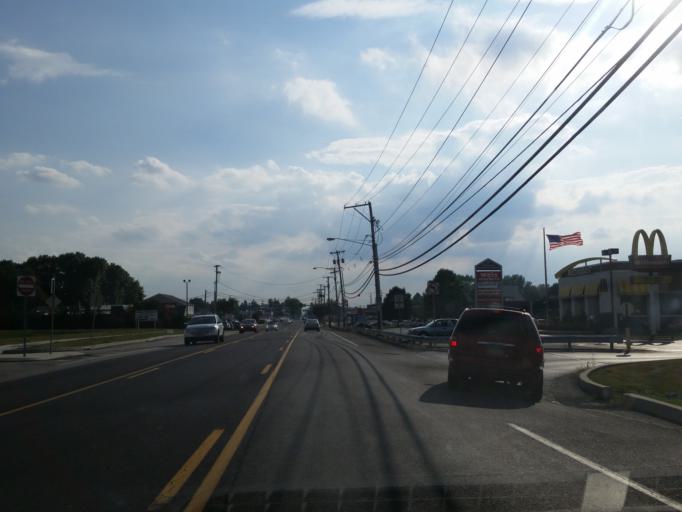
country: US
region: Pennsylvania
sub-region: Lebanon County
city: Palmyra
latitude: 40.3141
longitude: -76.5822
